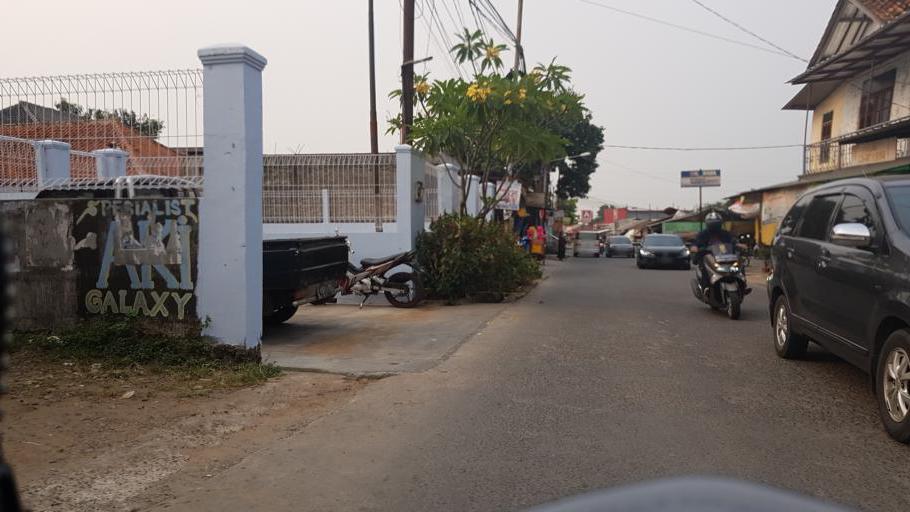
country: ID
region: West Java
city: Depok
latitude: -6.3671
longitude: 106.8430
